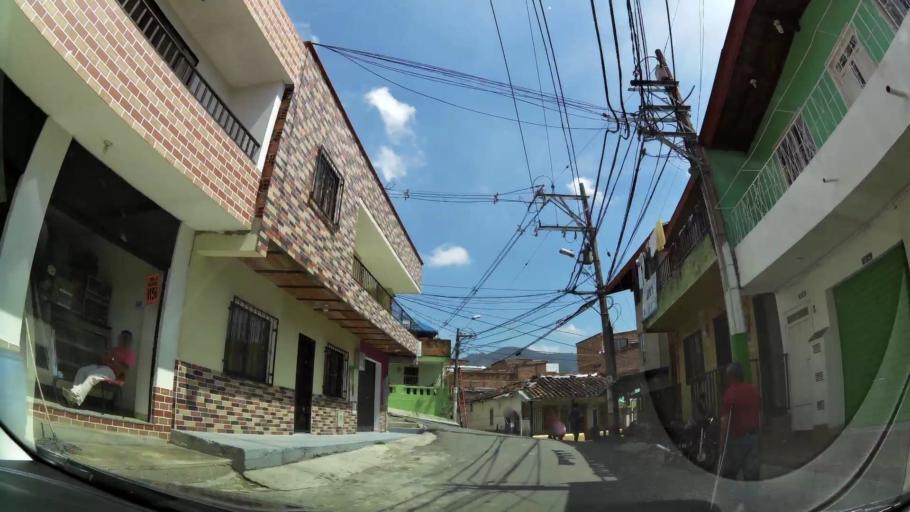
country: CO
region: Antioquia
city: La Estrella
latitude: 6.1848
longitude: -75.6589
